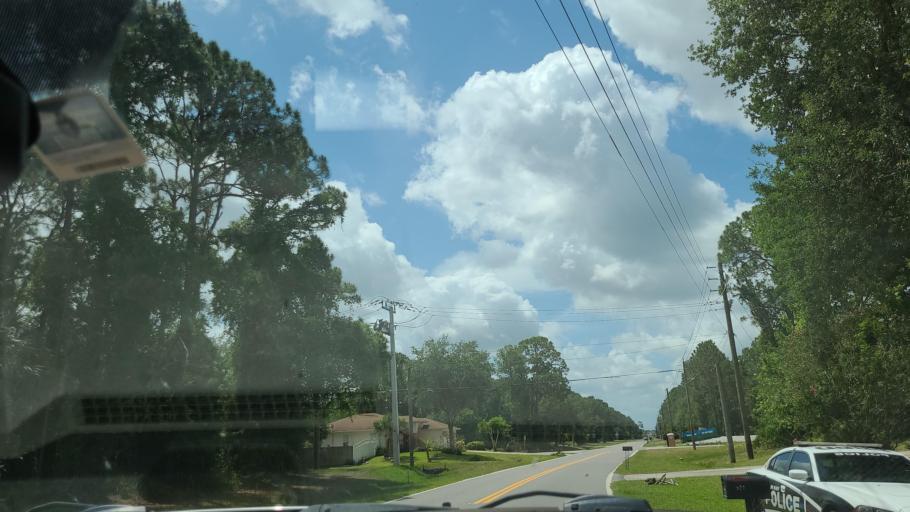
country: US
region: Florida
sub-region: Brevard County
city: June Park
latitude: 28.0071
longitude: -80.7167
